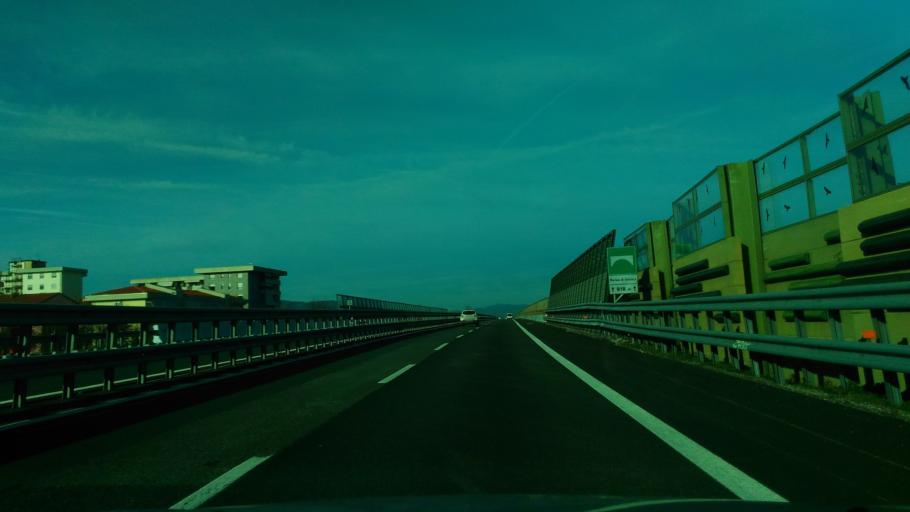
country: IT
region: Tuscany
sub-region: Provincia di Massa-Carrara
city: Marina di Carrara
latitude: 44.0434
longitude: 10.0519
